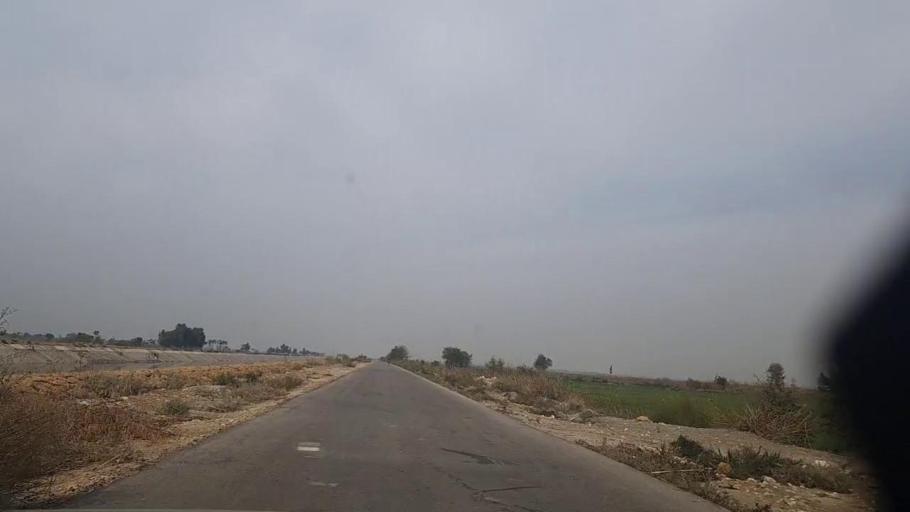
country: PK
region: Sindh
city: Sakrand
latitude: 26.2564
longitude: 68.2462
